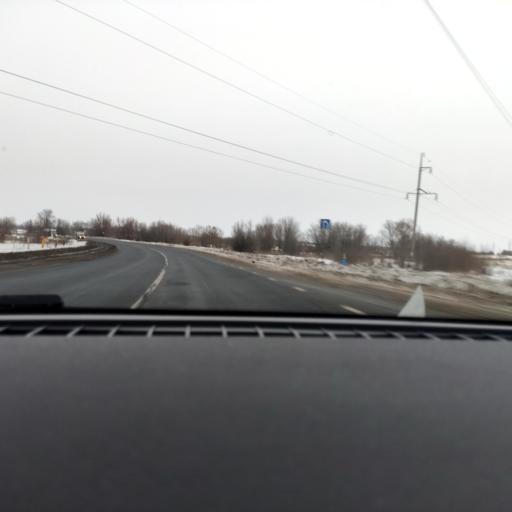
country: RU
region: Samara
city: Kinel'
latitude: 53.1498
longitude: 50.5111
